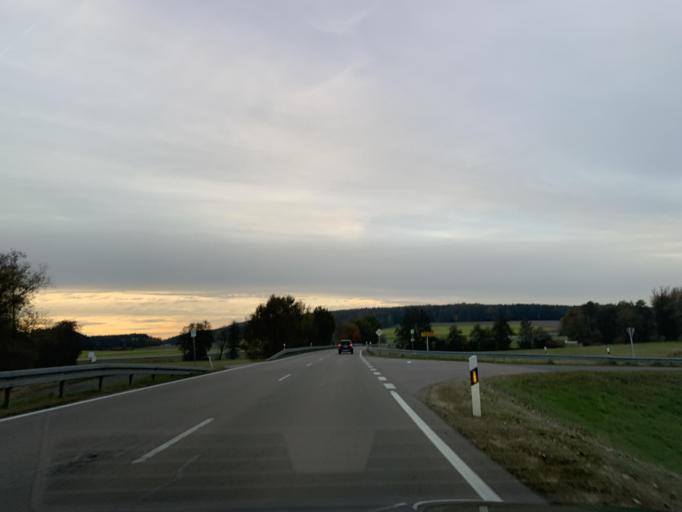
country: DE
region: Bavaria
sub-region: Upper Palatinate
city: Neunburg vorm Wald
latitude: 49.3543
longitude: 12.3766
